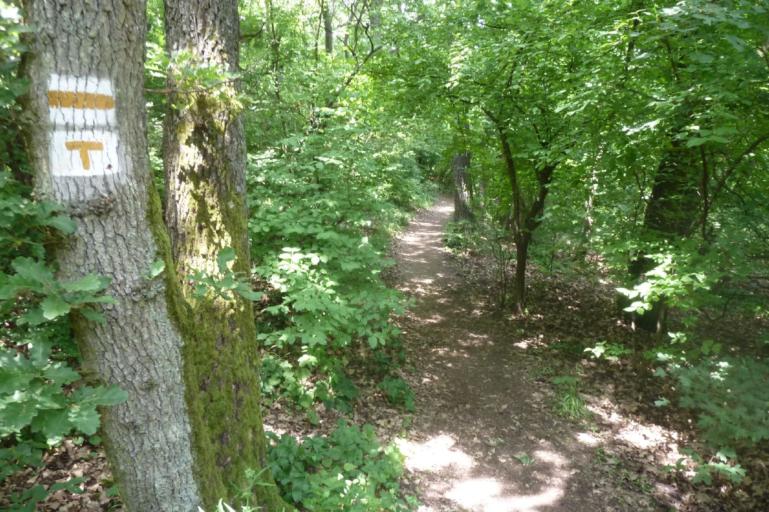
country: HU
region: Pest
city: Nagykovacsi
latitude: 47.6758
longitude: 19.0169
